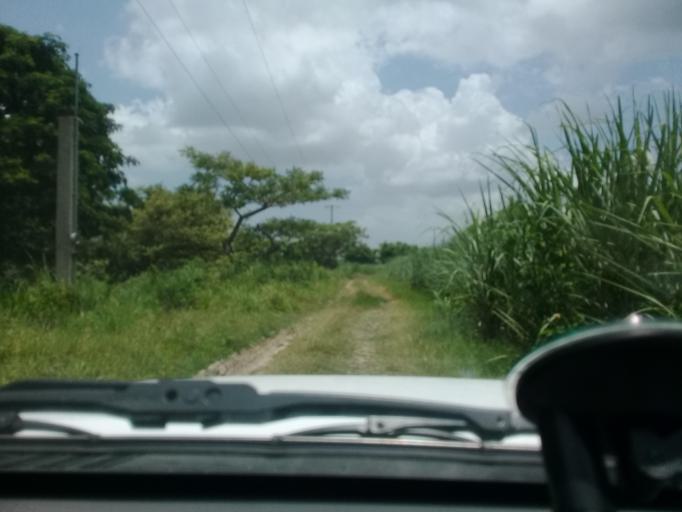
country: MX
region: Veracruz
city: Moralillo
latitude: 22.1351
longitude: -98.0402
